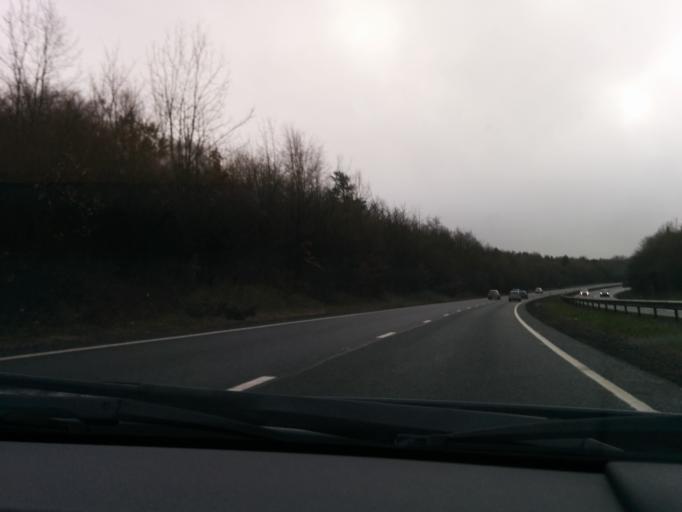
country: GB
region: England
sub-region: Hampshire
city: Highclere
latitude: 51.3394
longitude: -1.3406
